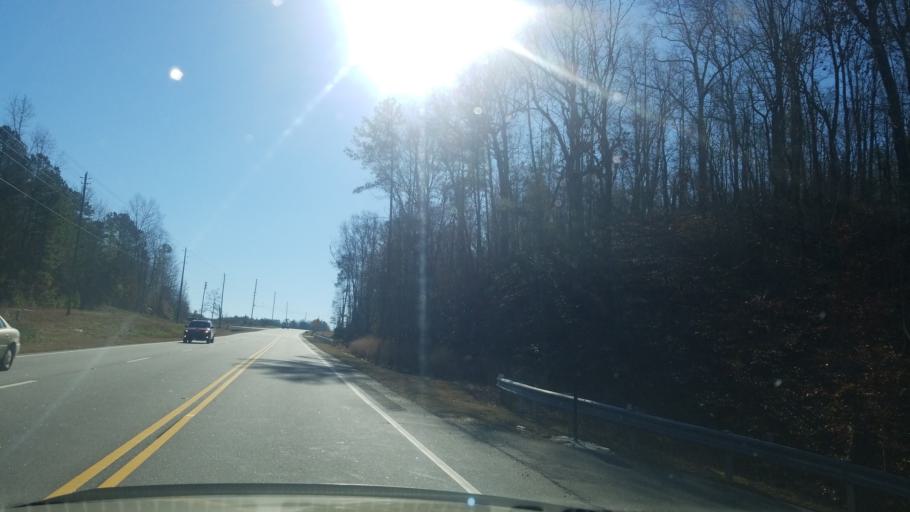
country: US
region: Georgia
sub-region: Troup County
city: West Point
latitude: 32.8590
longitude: -85.1335
